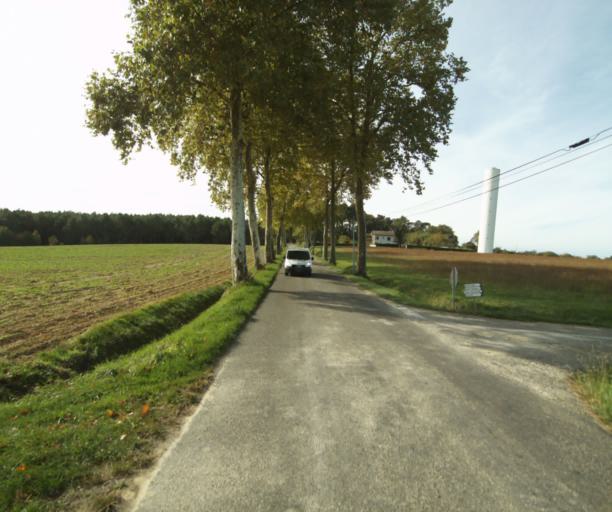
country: FR
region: Midi-Pyrenees
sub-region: Departement du Gers
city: Eauze
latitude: 43.9364
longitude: 0.0939
